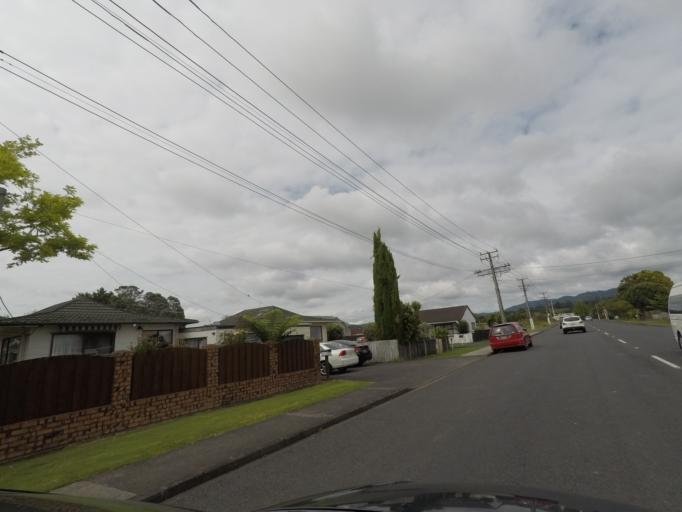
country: NZ
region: Auckland
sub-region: Auckland
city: Waitakere
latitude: -36.8991
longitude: 174.6239
